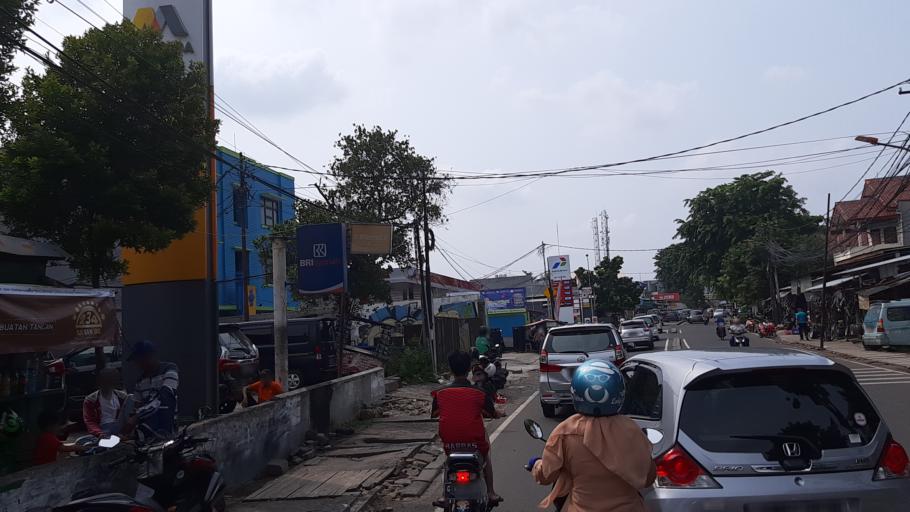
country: ID
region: Jakarta Raya
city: Jakarta
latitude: -6.2085
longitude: 106.7887
